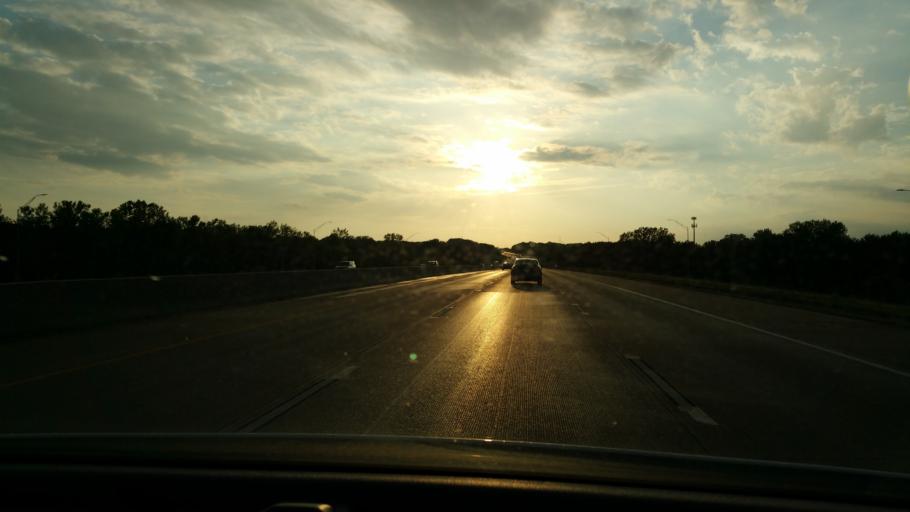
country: US
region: Iowa
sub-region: Polk County
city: Johnston
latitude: 41.6522
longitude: -93.6987
